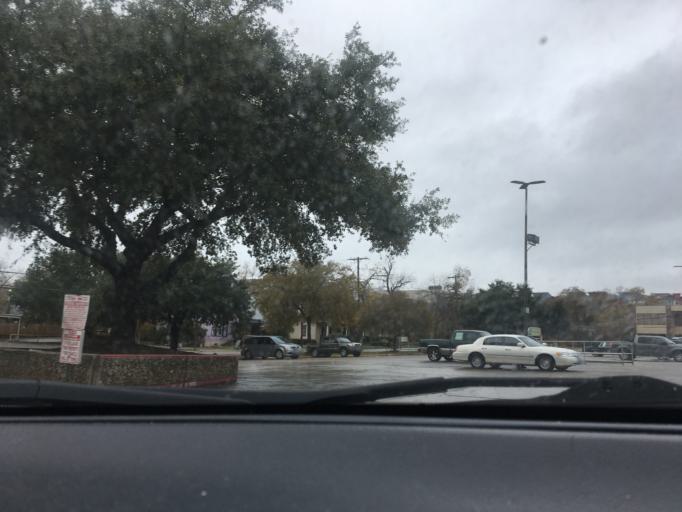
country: US
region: Texas
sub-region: Hays County
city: San Marcos
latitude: 29.8830
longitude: -97.9434
